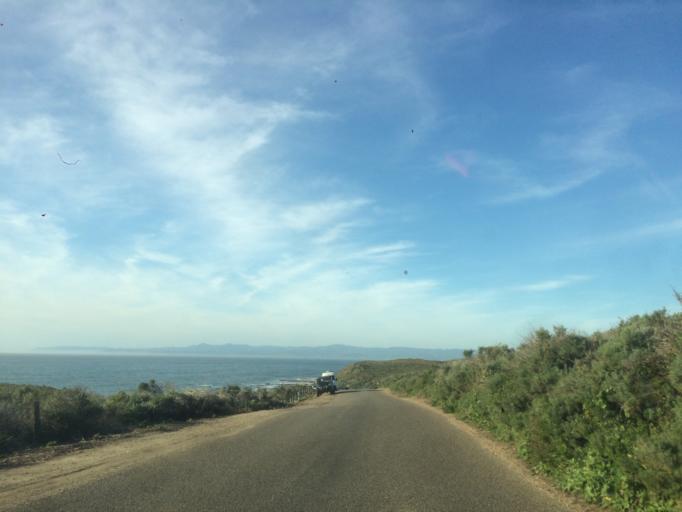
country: US
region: California
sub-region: San Luis Obispo County
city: Los Osos
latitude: 35.2716
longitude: -120.8884
